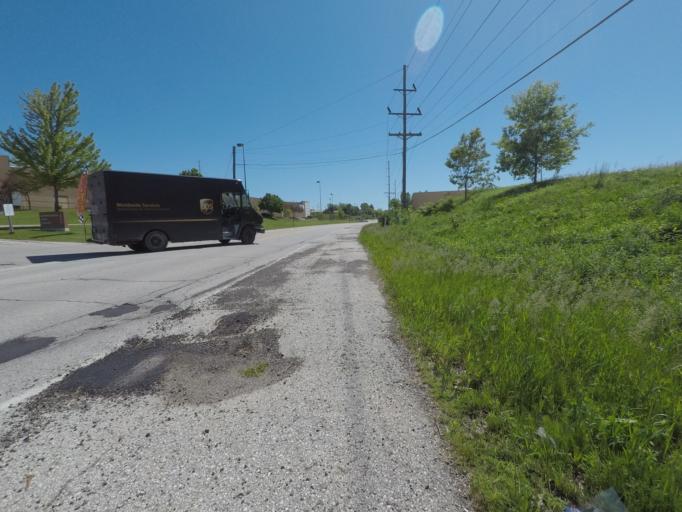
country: US
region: Wisconsin
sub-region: Sheboygan County
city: Kohler
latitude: 43.7519
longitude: -87.7542
